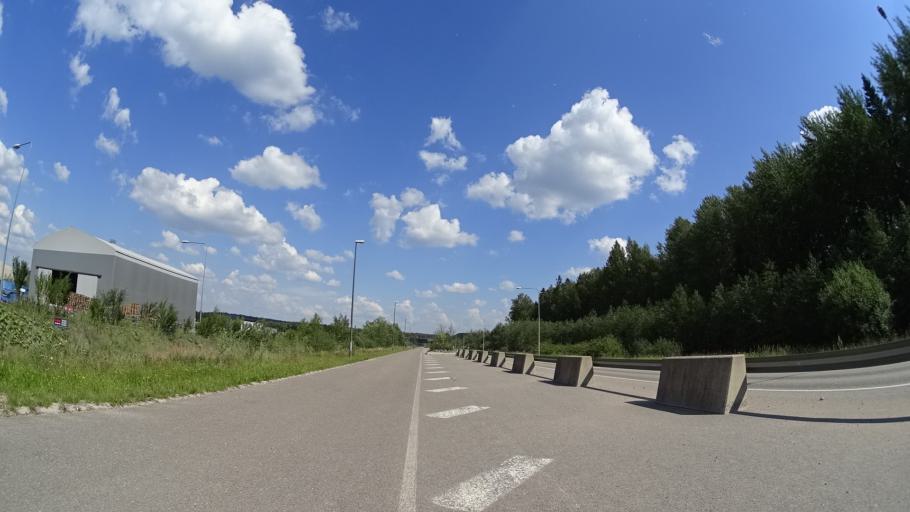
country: FI
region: Uusimaa
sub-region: Helsinki
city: Vantaa
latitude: 60.3278
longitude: 24.9209
